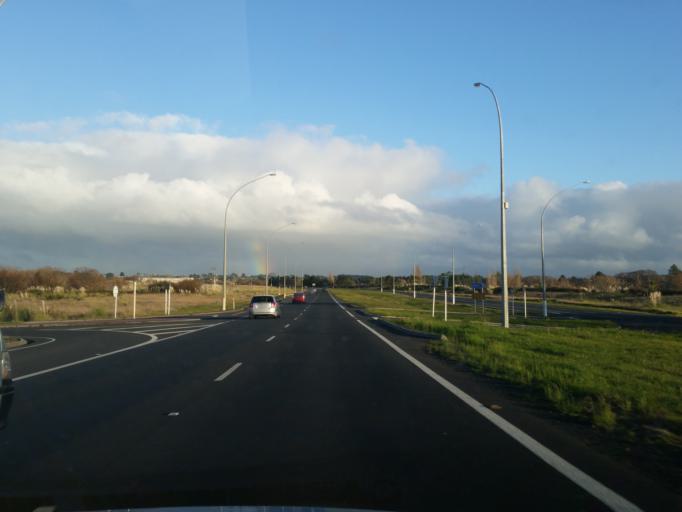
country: NZ
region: Waikato
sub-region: Waikato District
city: Te Kauwhata
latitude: -37.2953
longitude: 175.0599
